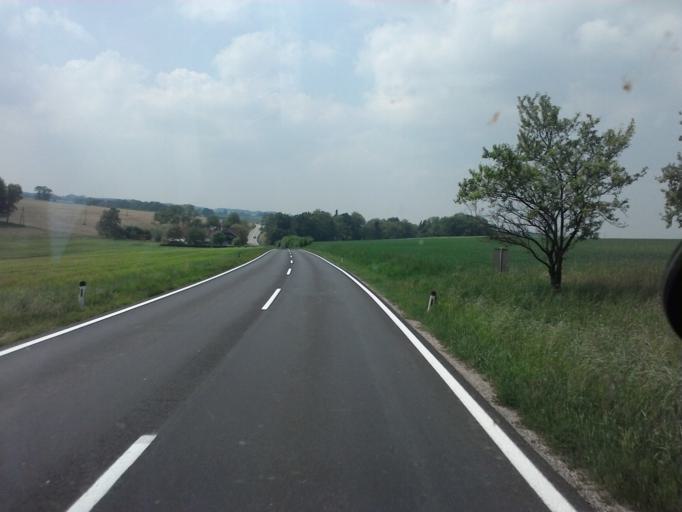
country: AT
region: Upper Austria
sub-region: Politischer Bezirk Kirchdorf an der Krems
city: Kremsmunster
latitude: 48.0653
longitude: 14.0955
